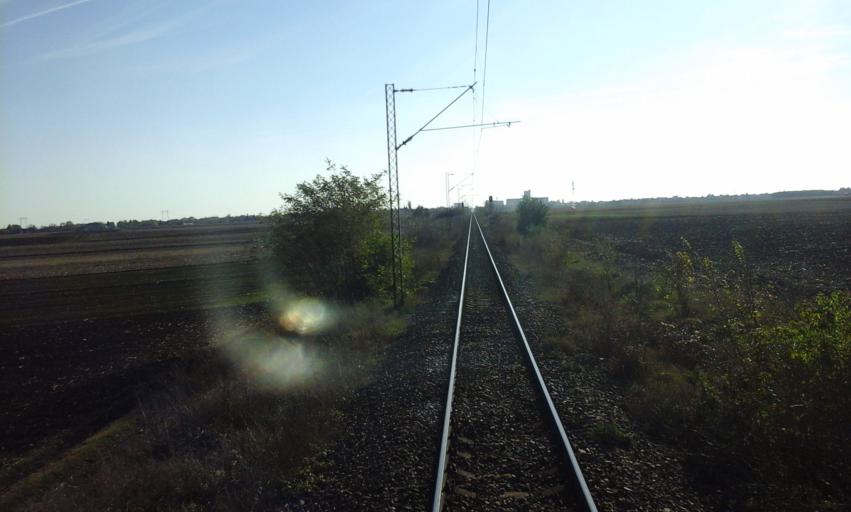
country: RS
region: Autonomna Pokrajina Vojvodina
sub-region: Severnobacki Okrug
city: Backa Topola
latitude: 45.8381
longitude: 19.6527
